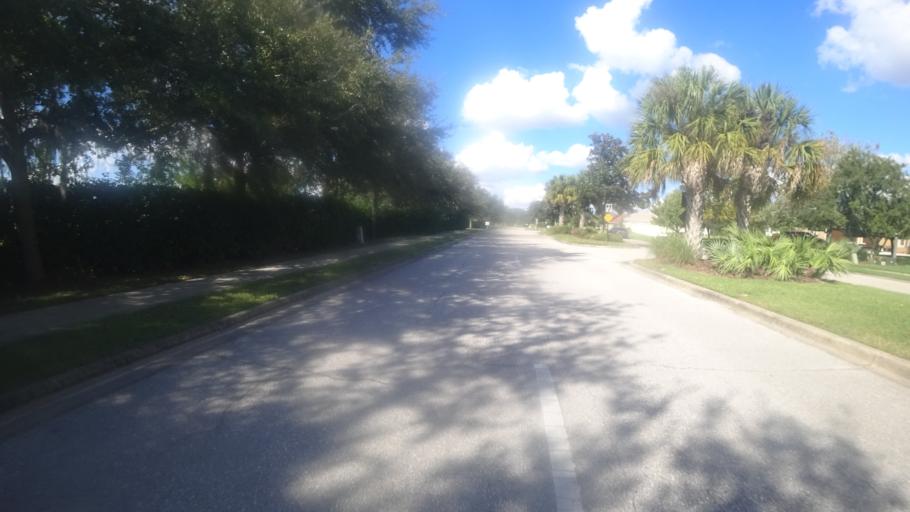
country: US
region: Florida
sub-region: Manatee County
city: Ellenton
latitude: 27.5341
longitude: -82.3922
